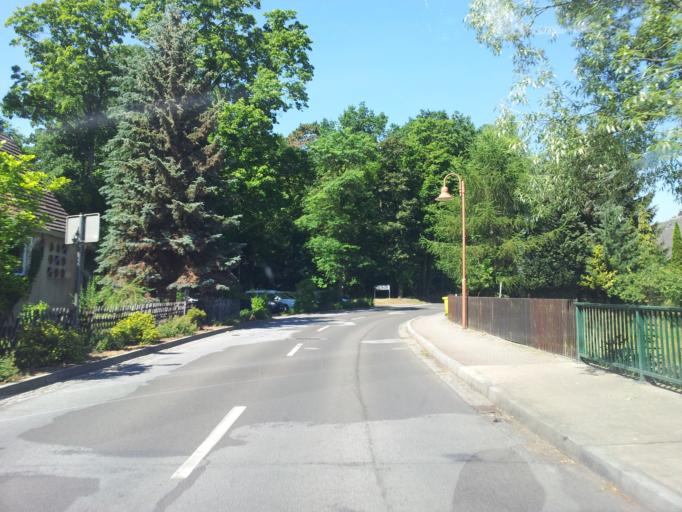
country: DE
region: Saxony
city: Konigsbruck
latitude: 51.2640
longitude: 13.8986
